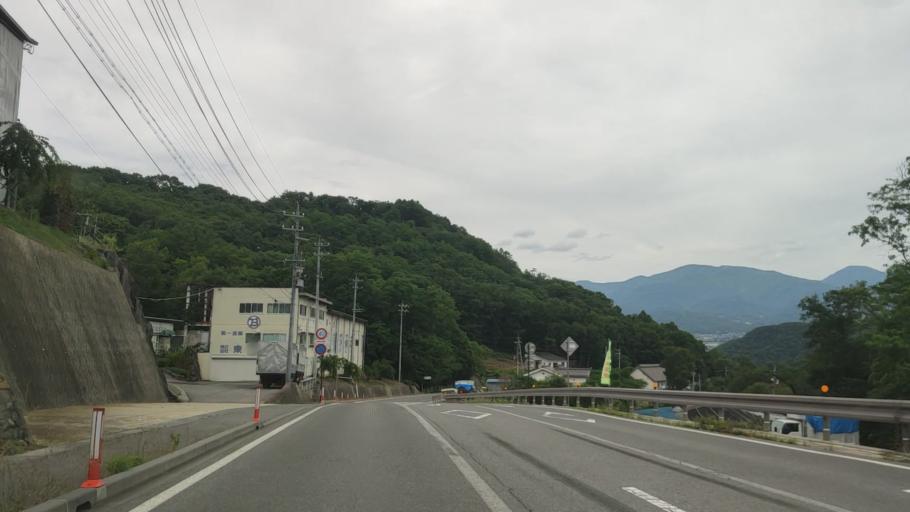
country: JP
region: Nagano
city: Kamimaruko
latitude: 36.3229
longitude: 138.3382
